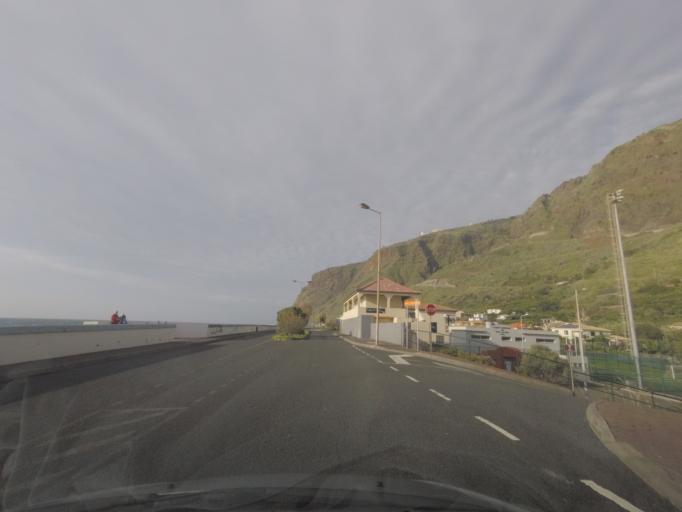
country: PT
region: Madeira
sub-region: Calheta
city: Faja da Ovelha
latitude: 32.7586
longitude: -17.2312
